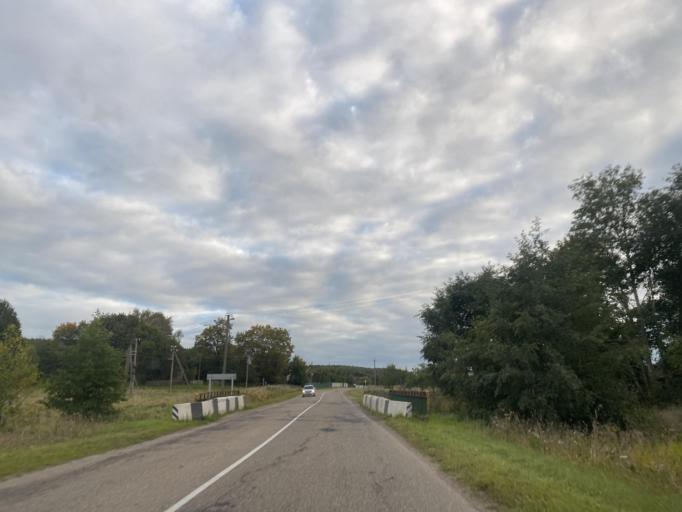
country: BY
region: Grodnenskaya
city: Kreva
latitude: 54.3051
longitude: 26.2786
